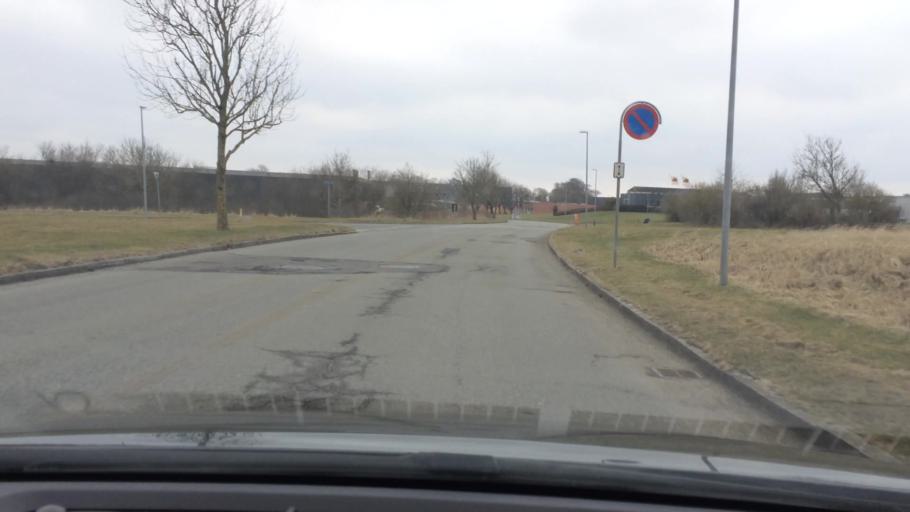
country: DK
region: South Denmark
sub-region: Vejle Kommune
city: Vejle
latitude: 55.7334
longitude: 9.5679
